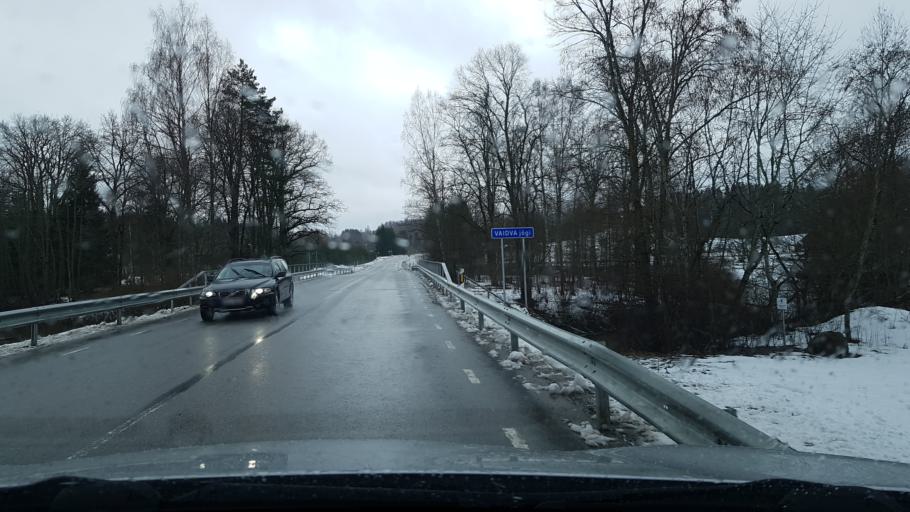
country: LV
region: Apes Novads
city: Ape
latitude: 57.5753
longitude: 26.6605
